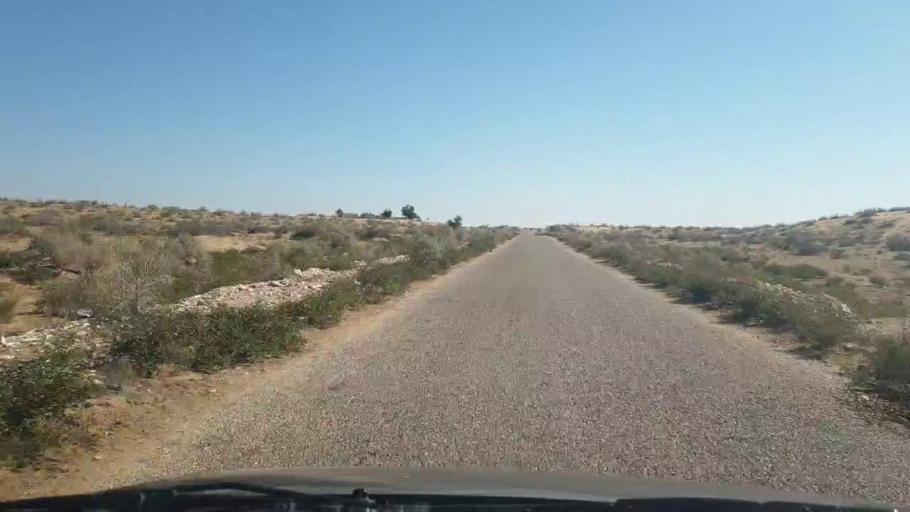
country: PK
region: Sindh
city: Bozdar
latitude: 27.0155
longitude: 68.7821
